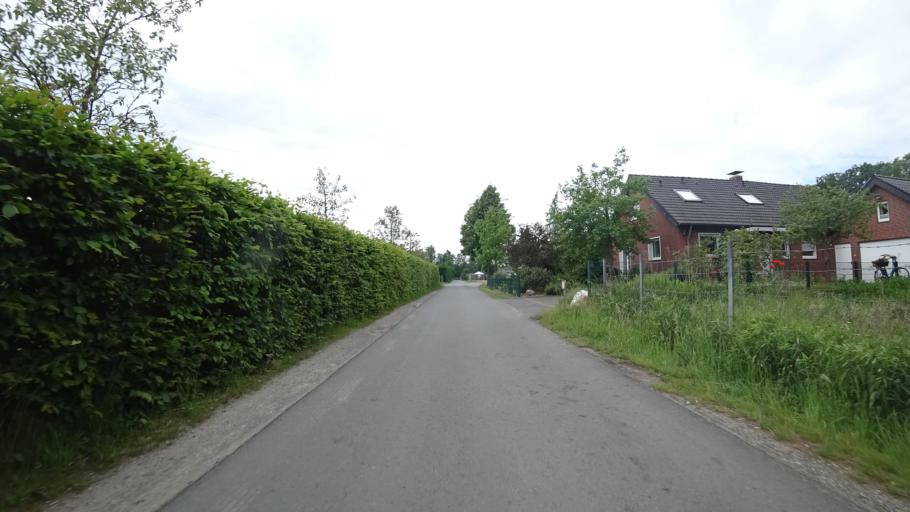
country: DE
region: North Rhine-Westphalia
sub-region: Regierungsbezirk Detmold
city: Guetersloh
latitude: 51.9123
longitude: 8.3361
